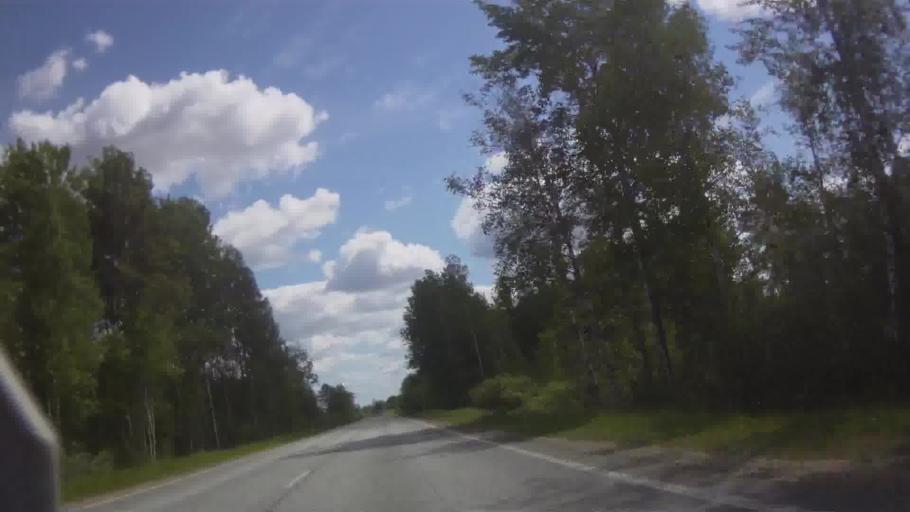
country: LV
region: Livani
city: Livani
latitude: 56.5264
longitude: 26.4061
